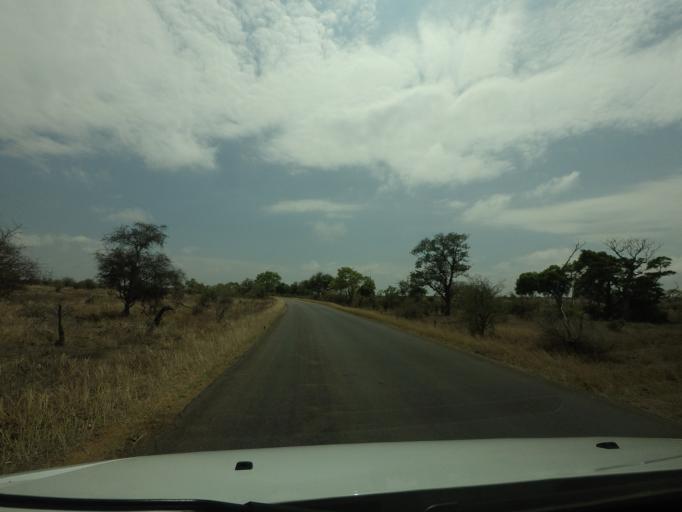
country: ZA
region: Limpopo
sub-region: Mopani District Municipality
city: Phalaborwa
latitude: -24.1652
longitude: 31.7199
